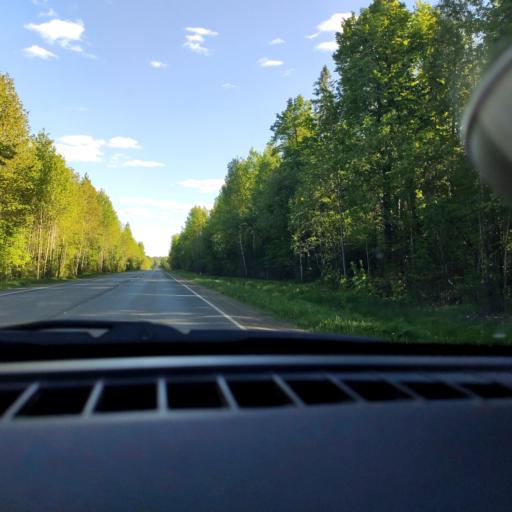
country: RU
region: Perm
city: Polazna
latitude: 58.2836
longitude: 56.1644
